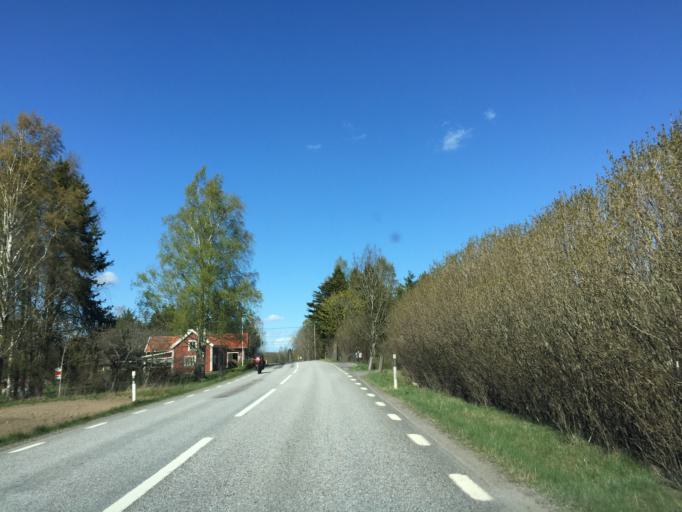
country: SE
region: OErebro
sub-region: Hallsbergs Kommun
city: Skollersta
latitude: 59.1037
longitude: 15.3270
